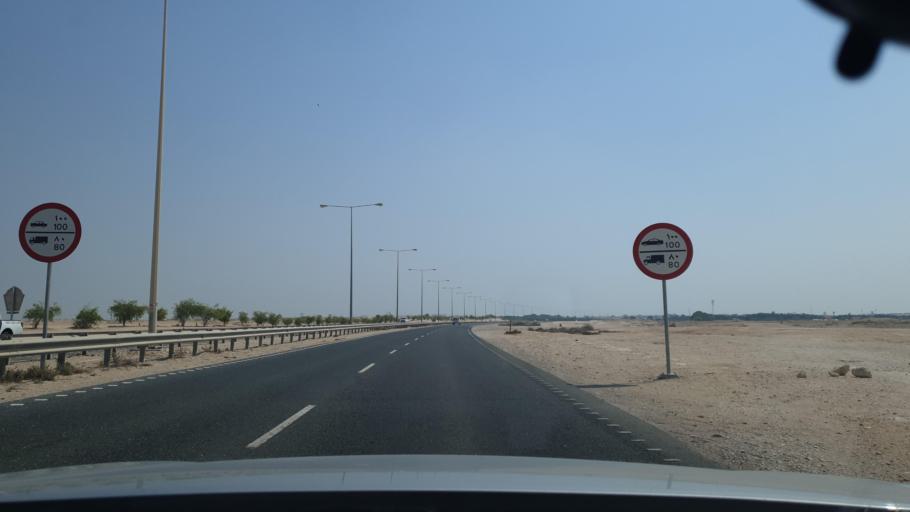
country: QA
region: Al Khawr
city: Al Khawr
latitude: 25.7387
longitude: 51.4888
